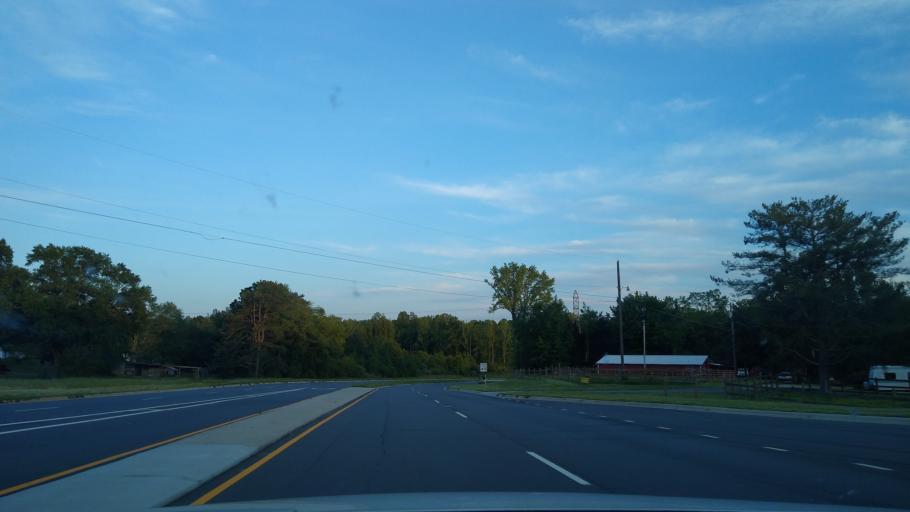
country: US
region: North Carolina
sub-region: Forsyth County
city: Kernersville
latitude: 36.1240
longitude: -80.0456
